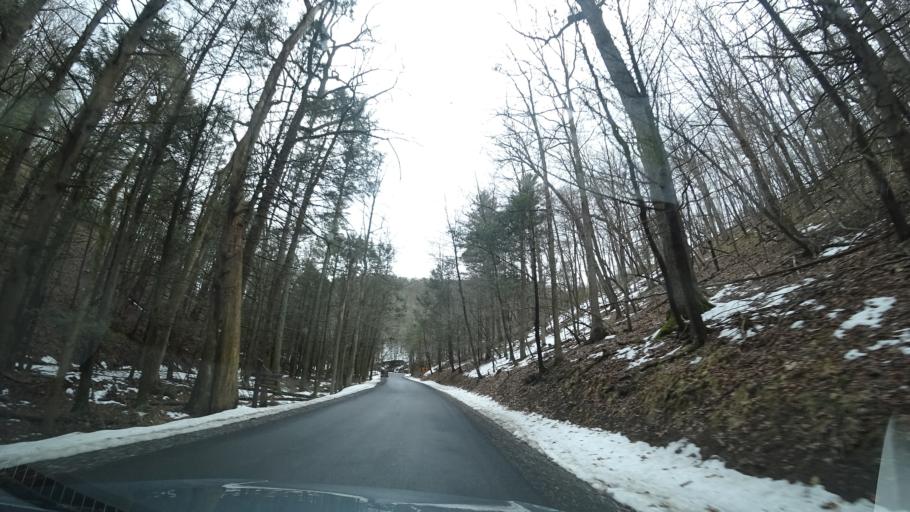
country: US
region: Virginia
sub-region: Shenandoah County
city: Basye
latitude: 38.8980
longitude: -78.9165
